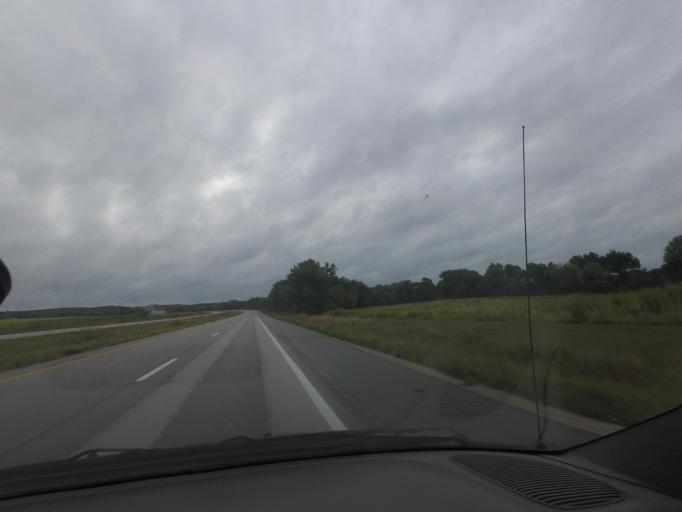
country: US
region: Missouri
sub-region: Shelby County
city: Shelbina
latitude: 39.6666
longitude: -91.9135
